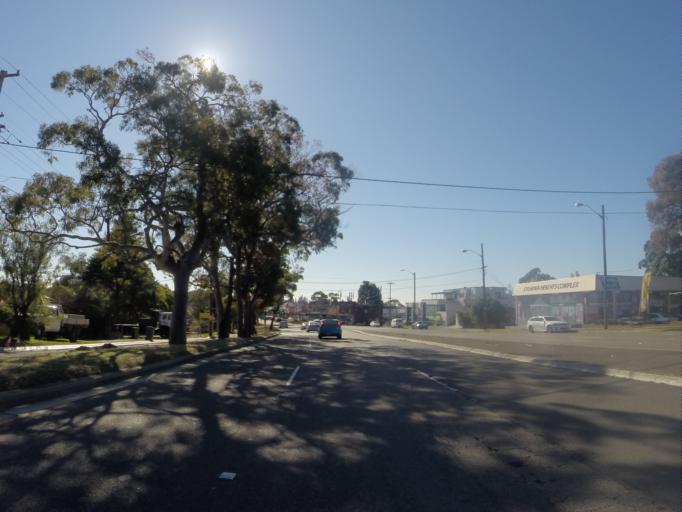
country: AU
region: New South Wales
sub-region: Sutherland Shire
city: Kareela
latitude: -34.0147
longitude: 151.0940
